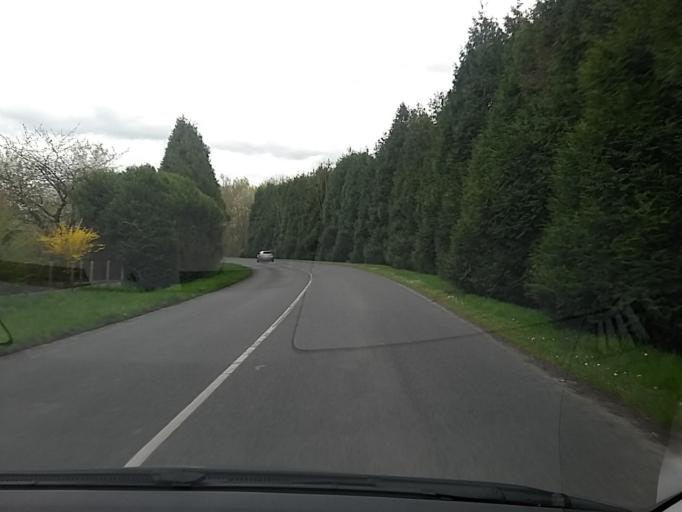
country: FR
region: Picardie
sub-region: Departement de l'Oise
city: Longueil-Sainte-Marie
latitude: 49.3469
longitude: 2.7325
